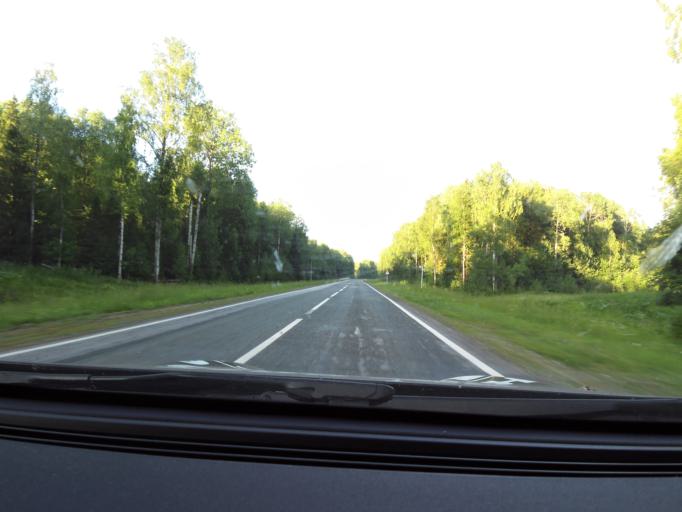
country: RU
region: Kirov
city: Kostino
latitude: 58.6407
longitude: 53.8180
